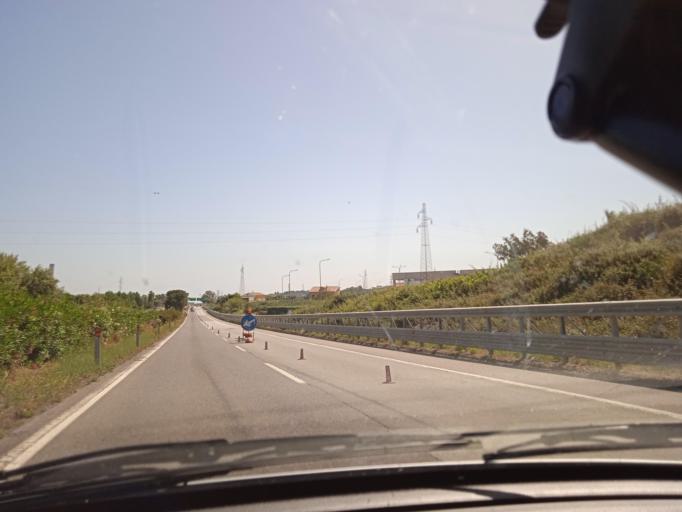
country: IT
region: Sicily
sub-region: Messina
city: San Filippo del Mela
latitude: 38.1881
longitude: 15.2662
